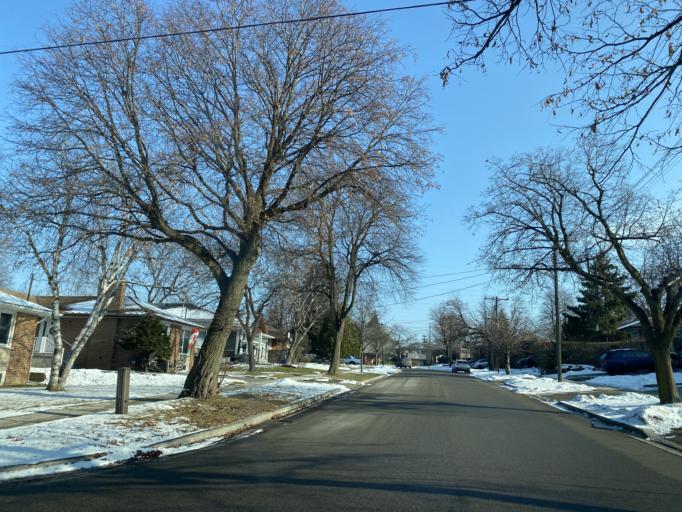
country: CA
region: Ontario
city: Etobicoke
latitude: 43.6709
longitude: -79.5644
